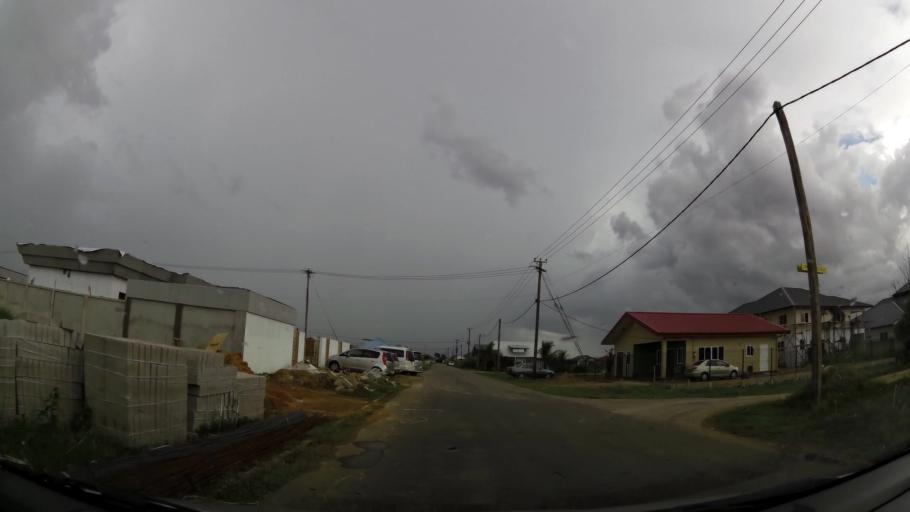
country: SR
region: Commewijne
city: Nieuw Amsterdam
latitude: 5.8519
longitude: -55.1149
